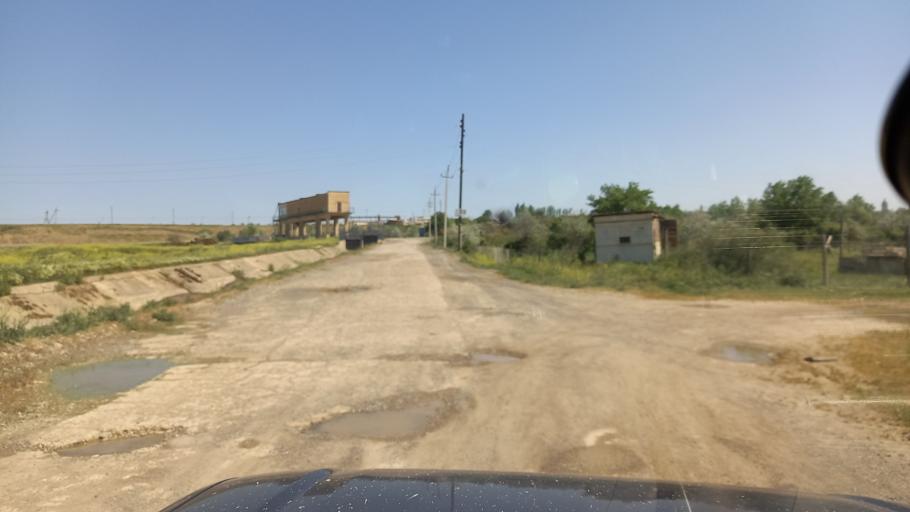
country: RU
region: Dagestan
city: Novaya Maka
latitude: 41.8091
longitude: 48.4081
